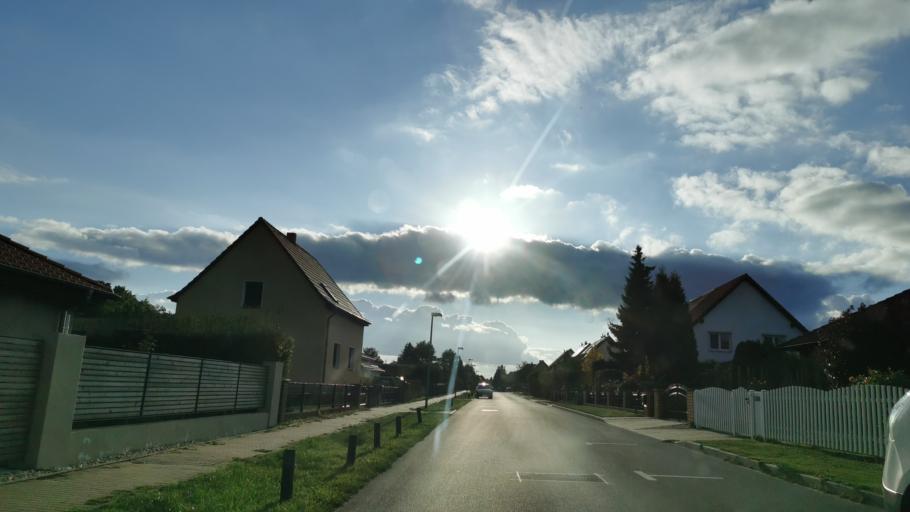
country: DE
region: Brandenburg
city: Werder
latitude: 52.3576
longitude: 12.9034
